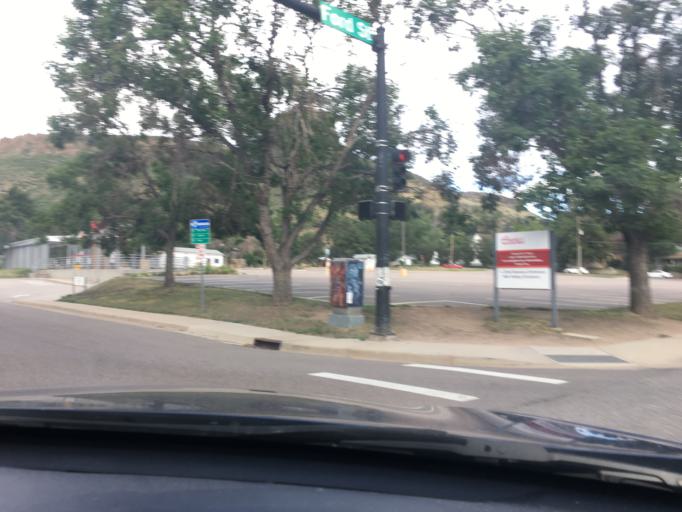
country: US
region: Colorado
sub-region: Jefferson County
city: Golden
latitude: 39.7558
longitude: -105.2184
